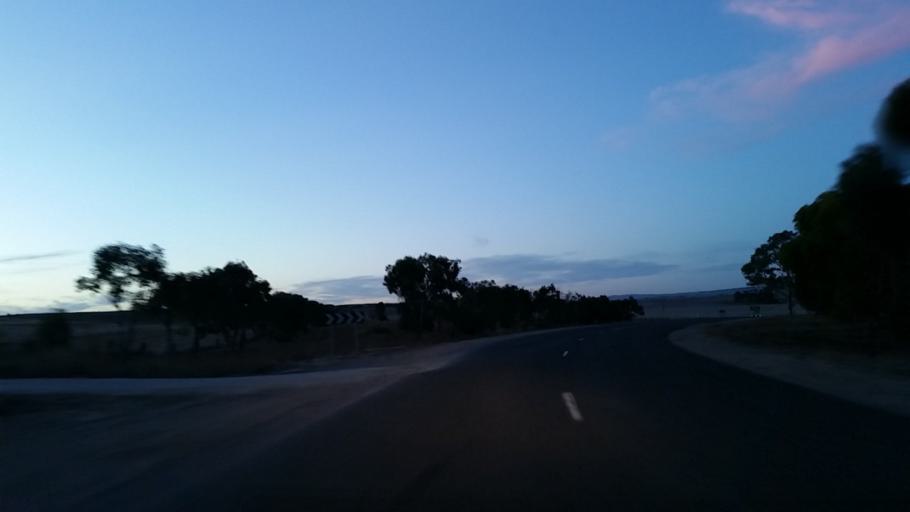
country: AU
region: South Australia
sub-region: Mount Barker
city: Callington
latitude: -35.1088
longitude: 139.0374
